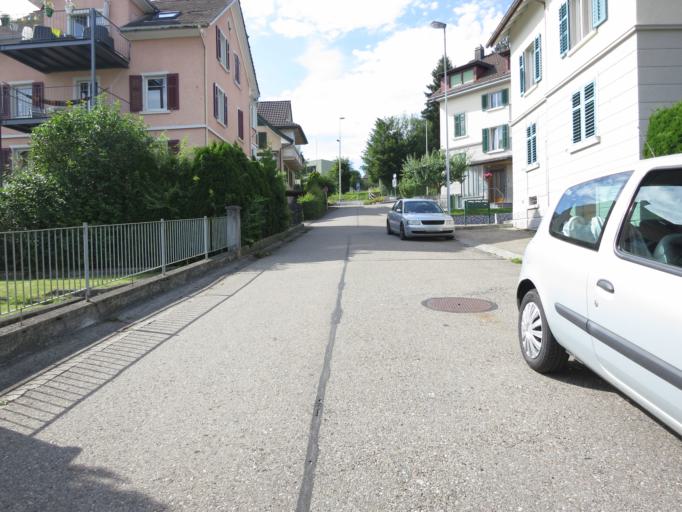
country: CH
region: Zurich
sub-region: Bezirk Hinwil
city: Rueti / Westlicher Dorfteil
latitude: 47.2592
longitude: 8.8462
